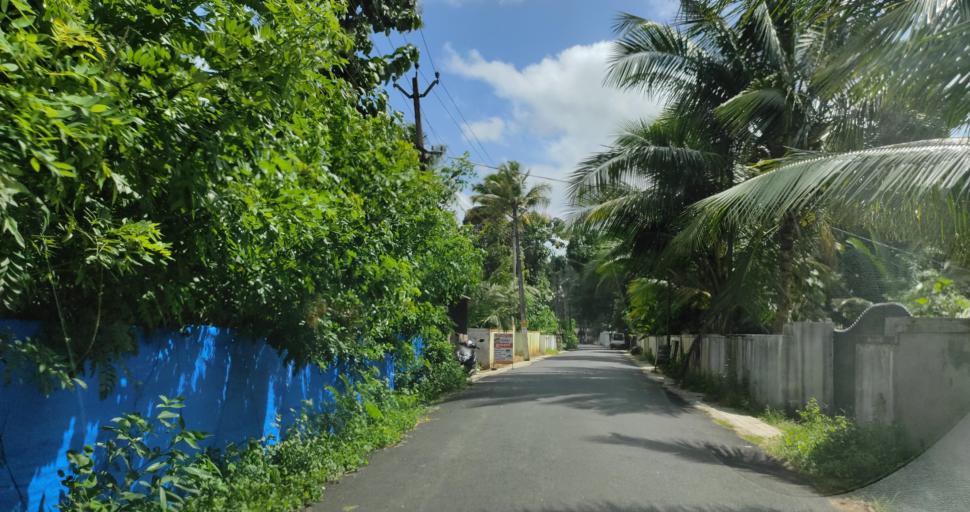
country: IN
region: Kerala
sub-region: Alappuzha
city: Shertallai
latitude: 9.6584
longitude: 76.3713
